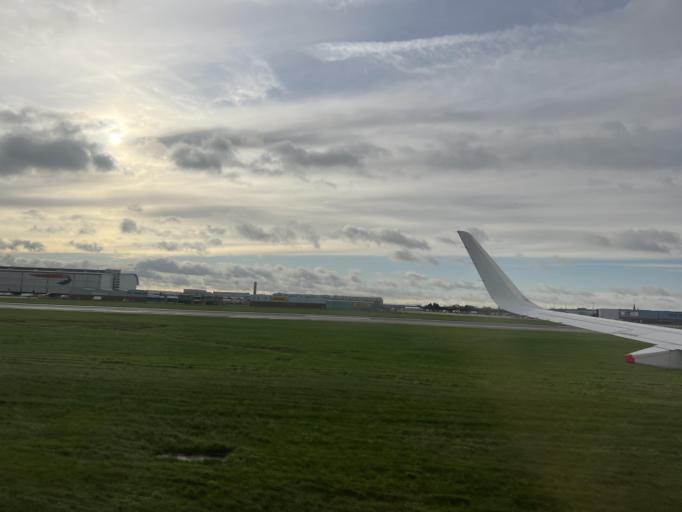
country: GB
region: England
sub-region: Greater London
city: West Drayton
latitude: 51.4665
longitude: -0.4714
